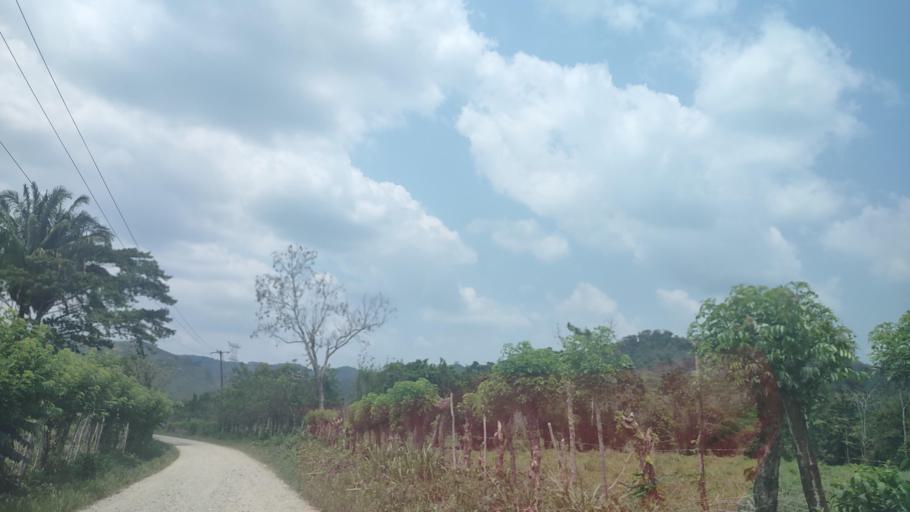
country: MX
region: Chiapas
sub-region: Tecpatan
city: Raudales Malpaso
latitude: 17.2753
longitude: -93.8713
